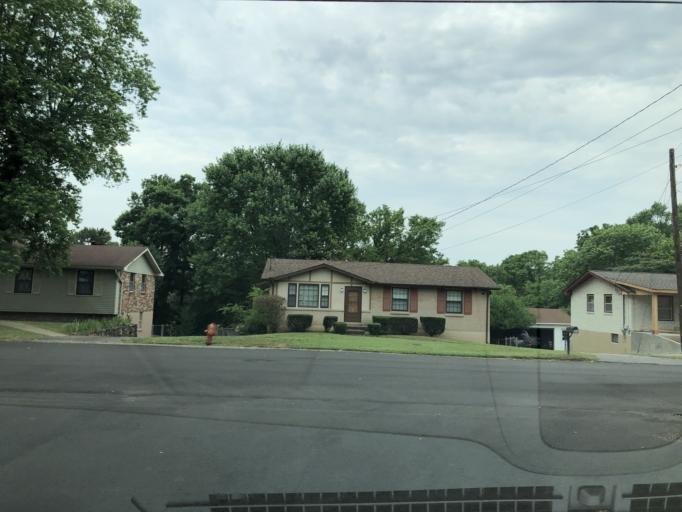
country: US
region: Tennessee
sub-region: Davidson County
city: Oak Hill
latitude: 36.0774
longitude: -86.6861
